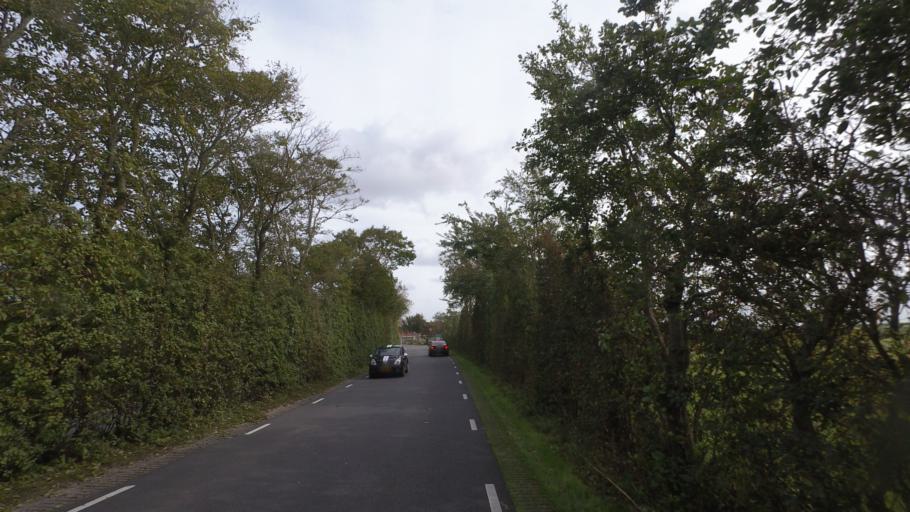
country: NL
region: Friesland
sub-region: Gemeente Ameland
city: Nes
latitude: 53.4471
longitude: 5.7914
